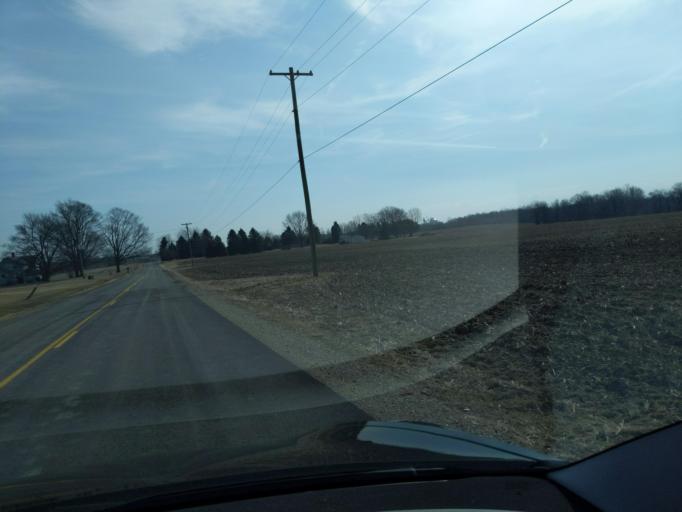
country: US
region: Michigan
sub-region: Ingham County
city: Williamston
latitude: 42.6593
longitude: -84.2539
